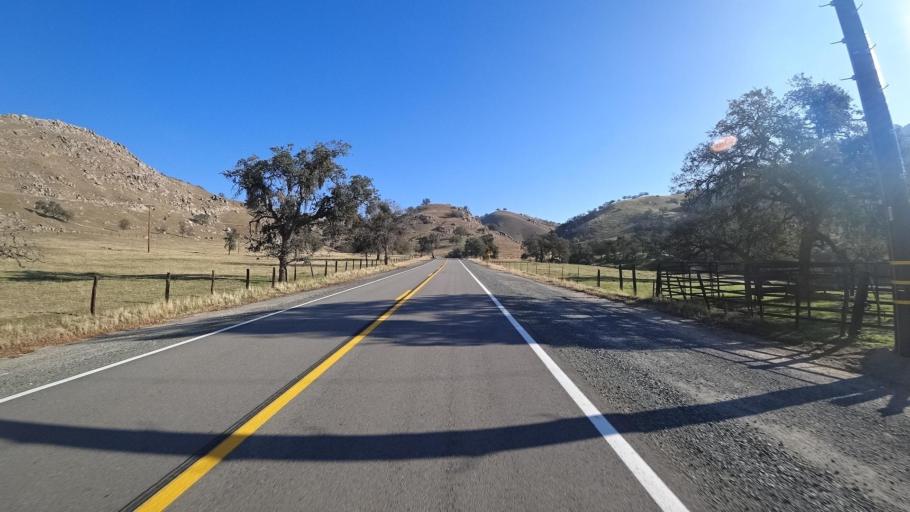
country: US
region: California
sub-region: Kern County
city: Alta Sierra
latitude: 35.7065
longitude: -118.8286
